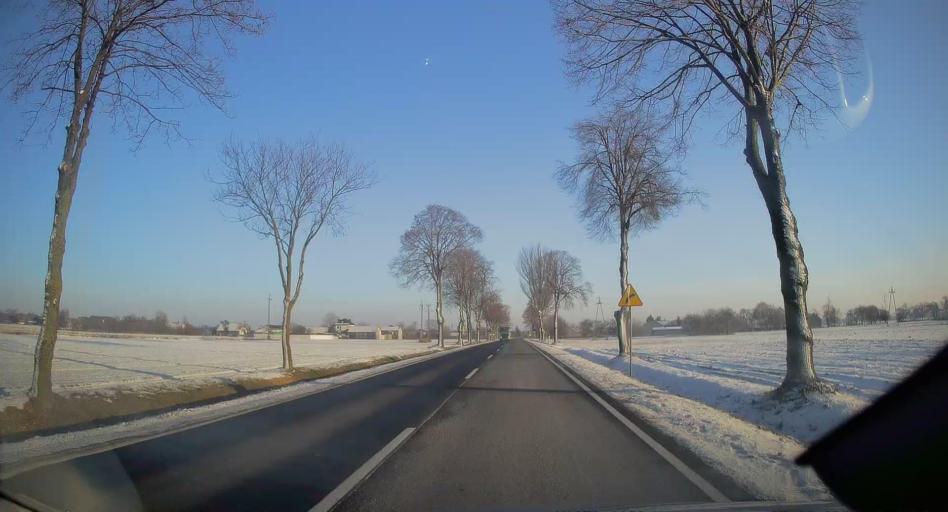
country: PL
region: Lodz Voivodeship
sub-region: Powiat opoczynski
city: Mniszkow
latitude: 51.3317
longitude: 20.0251
